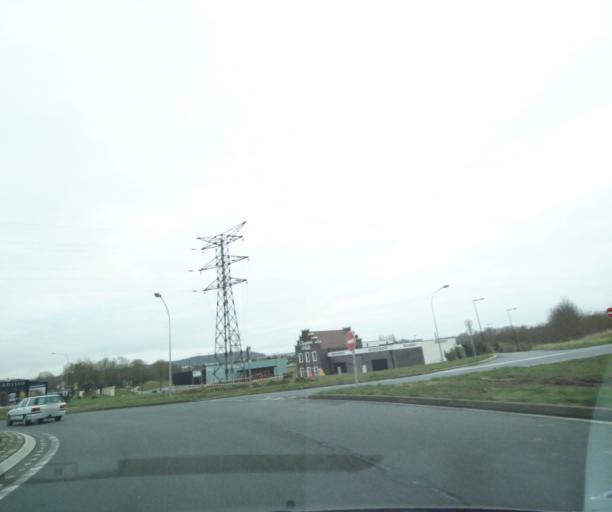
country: FR
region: Picardie
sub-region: Departement de l'Oise
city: Noyon
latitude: 49.5689
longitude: 2.9802
